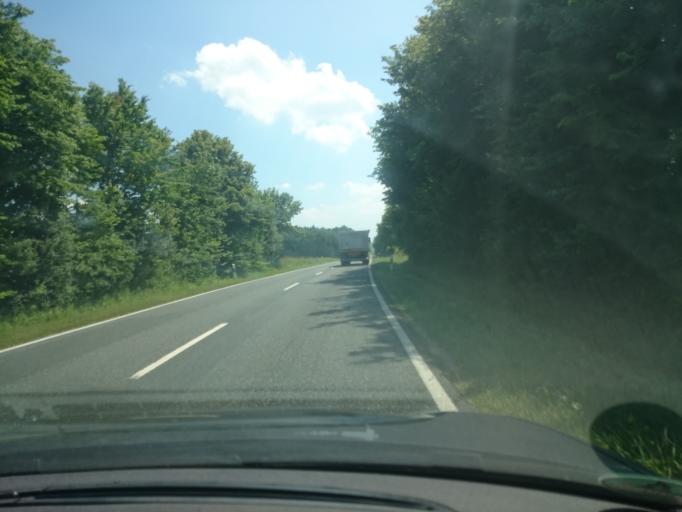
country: DE
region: Bavaria
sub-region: Regierungsbezirk Mittelfranken
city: Hilpoltstein
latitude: 49.1791
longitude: 11.2256
